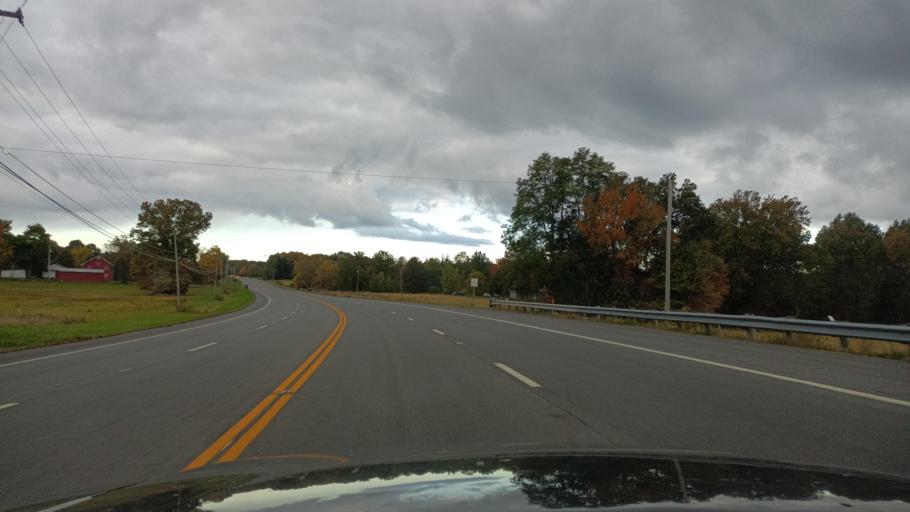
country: US
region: Ohio
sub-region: Trumbull County
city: Lordstown
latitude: 41.2016
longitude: -80.8508
